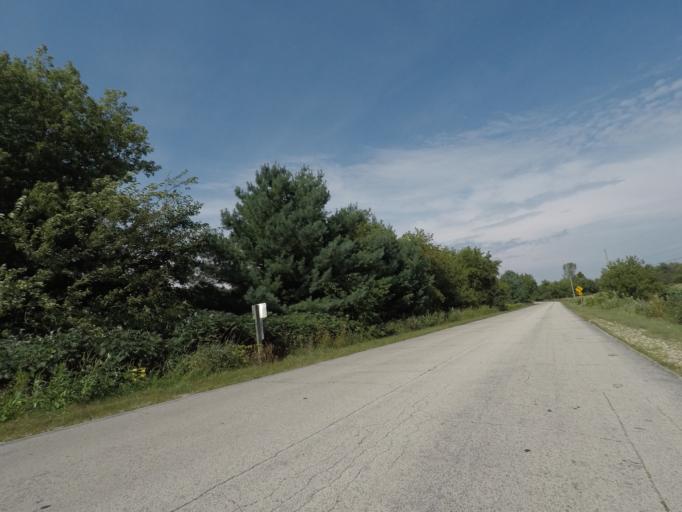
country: US
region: Wisconsin
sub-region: Jefferson County
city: Fort Atkinson
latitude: 42.8919
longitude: -88.8682
